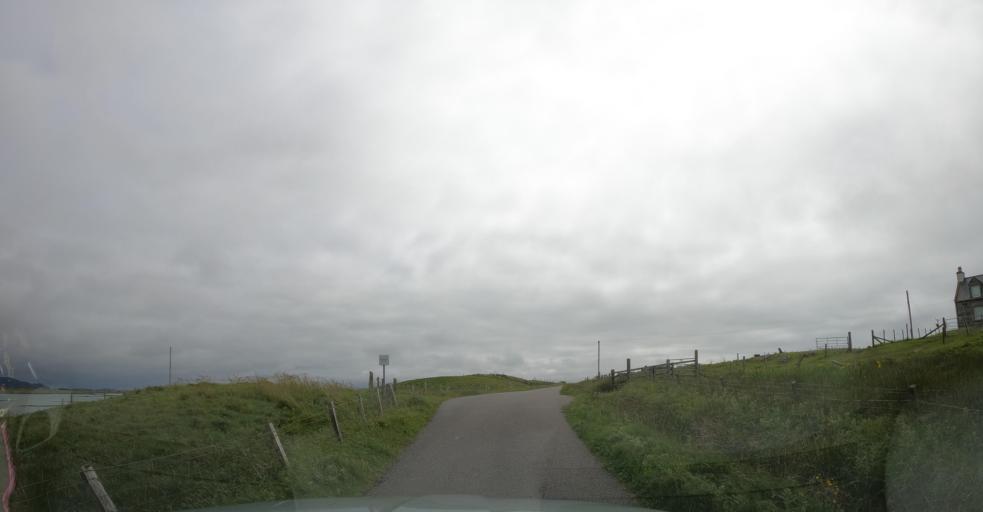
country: GB
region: Scotland
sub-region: Eilean Siar
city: Isle of North Uist
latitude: 57.5387
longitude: -7.3528
